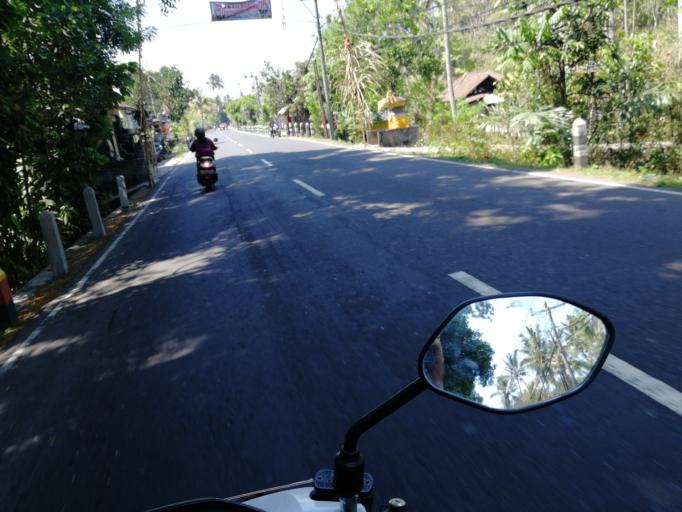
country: ID
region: Bali
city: Abang
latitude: -8.3971
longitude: 115.5963
